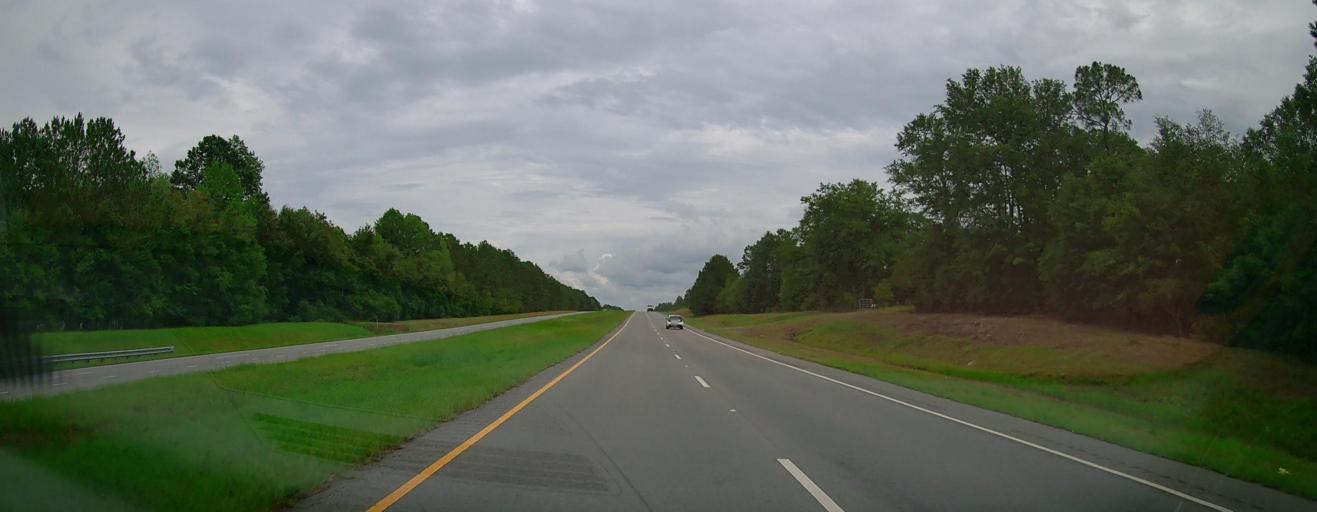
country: US
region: Georgia
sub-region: Telfair County
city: Helena
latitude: 32.0966
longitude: -82.9494
